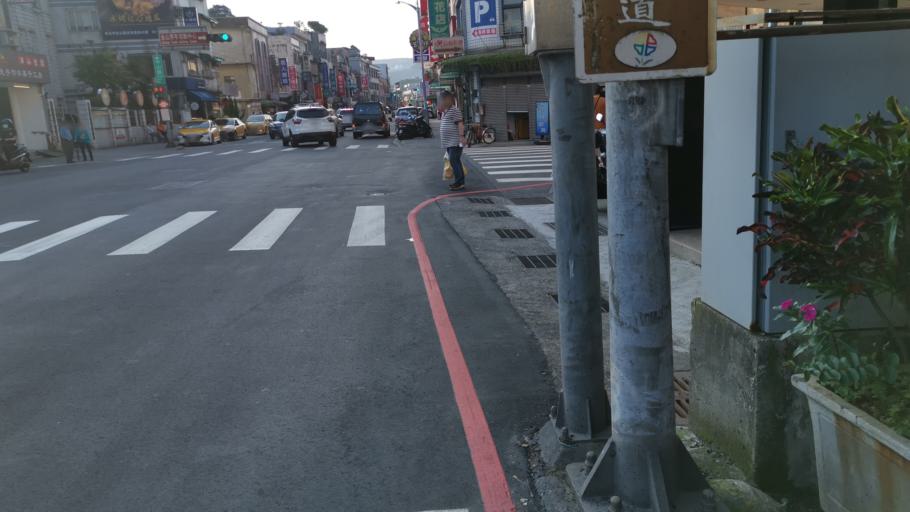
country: TW
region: Taiwan
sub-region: Keelung
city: Keelung
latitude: 25.2192
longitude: 121.6399
